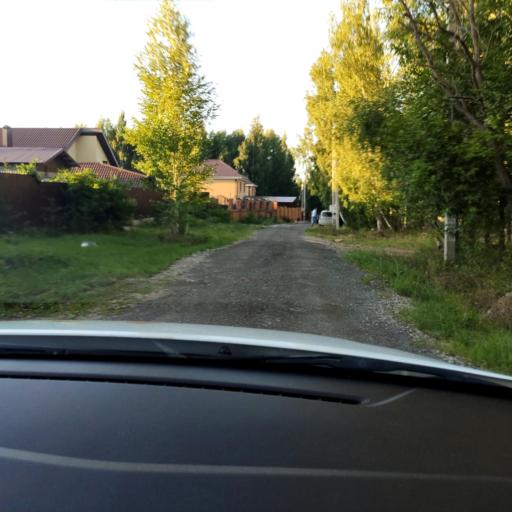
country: RU
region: Tatarstan
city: Stolbishchi
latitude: 55.7391
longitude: 49.2554
